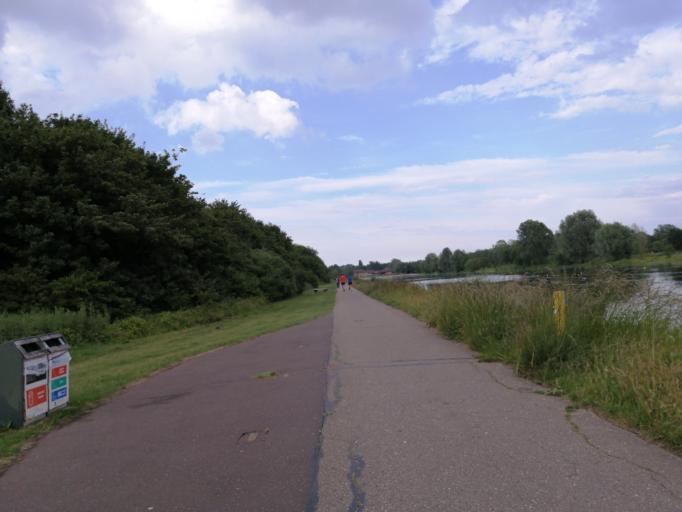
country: GB
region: England
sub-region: Peterborough
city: Peterborough
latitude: 52.5662
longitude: -0.2752
